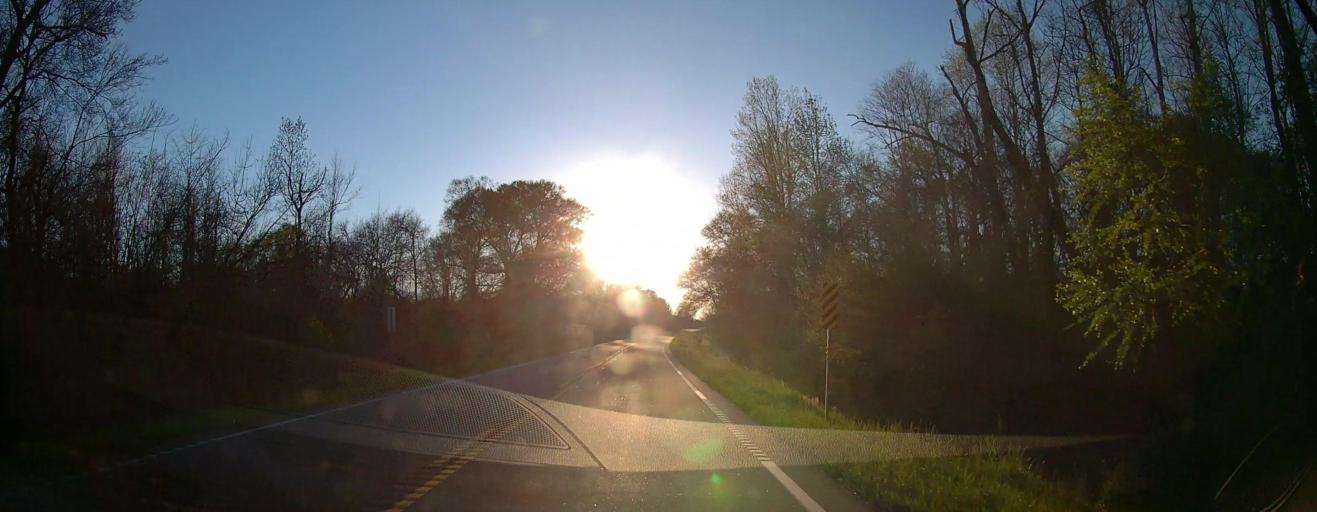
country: US
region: Georgia
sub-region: Crisp County
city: Cordele
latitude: 31.9569
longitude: -83.6226
